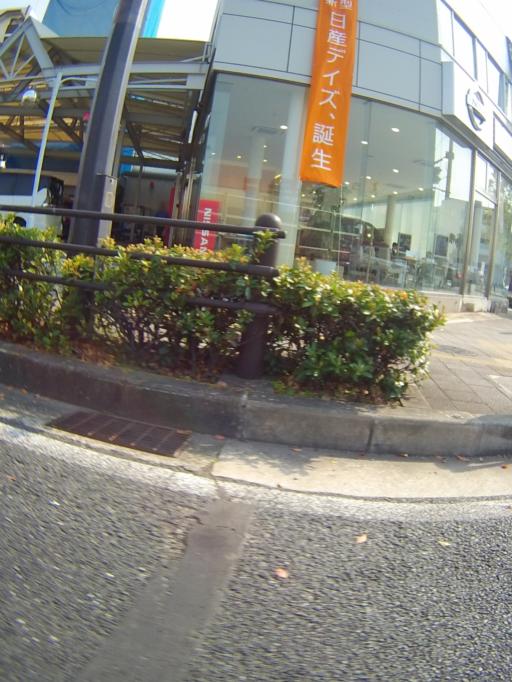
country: JP
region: Osaka
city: Osaka-shi
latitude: 34.6521
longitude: 135.4905
